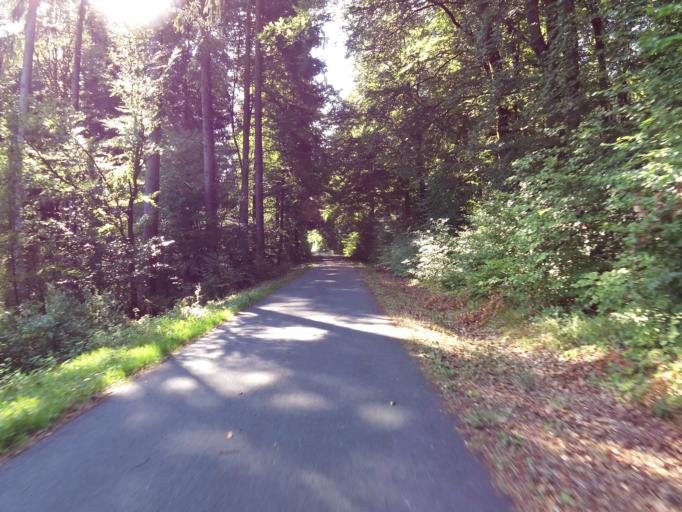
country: DE
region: Baden-Wuerttemberg
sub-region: Karlsruhe Region
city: Limbach
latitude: 49.4971
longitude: 9.2177
